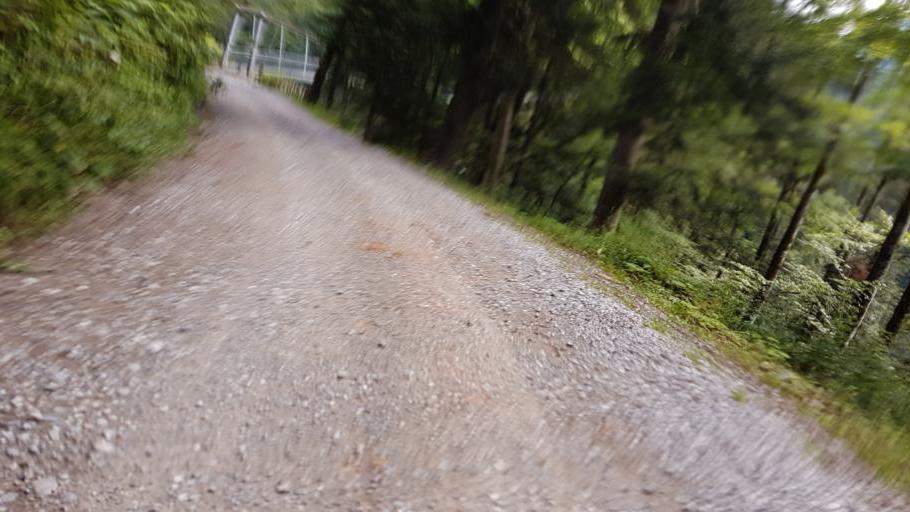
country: CH
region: Bern
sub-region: Obersimmental-Saanen District
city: Boltigen
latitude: 46.6724
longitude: 7.4621
